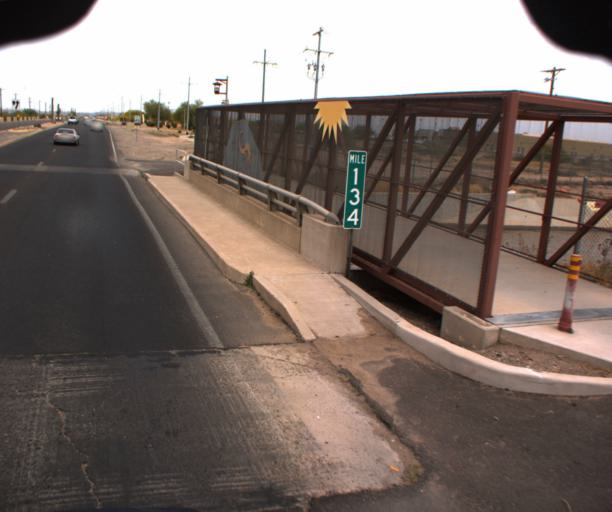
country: US
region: Arizona
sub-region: Pinal County
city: Coolidge
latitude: 32.9914
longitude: -111.5239
